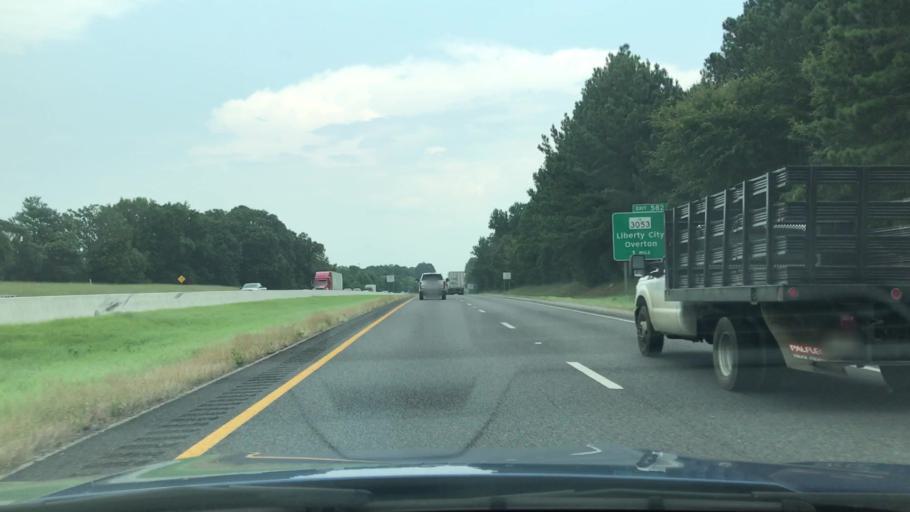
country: US
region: Texas
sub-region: Gregg County
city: Liberty City
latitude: 32.4354
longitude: -94.9640
